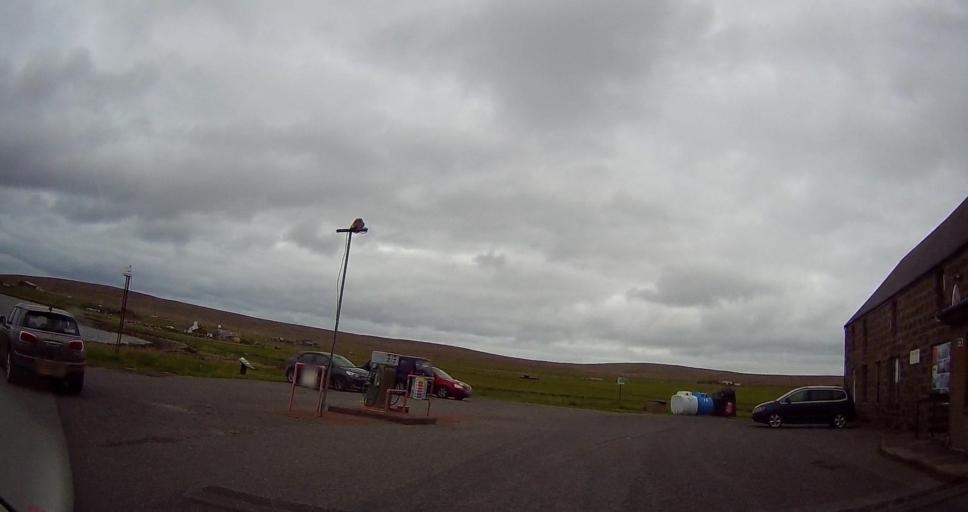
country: GB
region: Scotland
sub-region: Shetland Islands
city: Shetland
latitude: 60.7575
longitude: -0.8603
